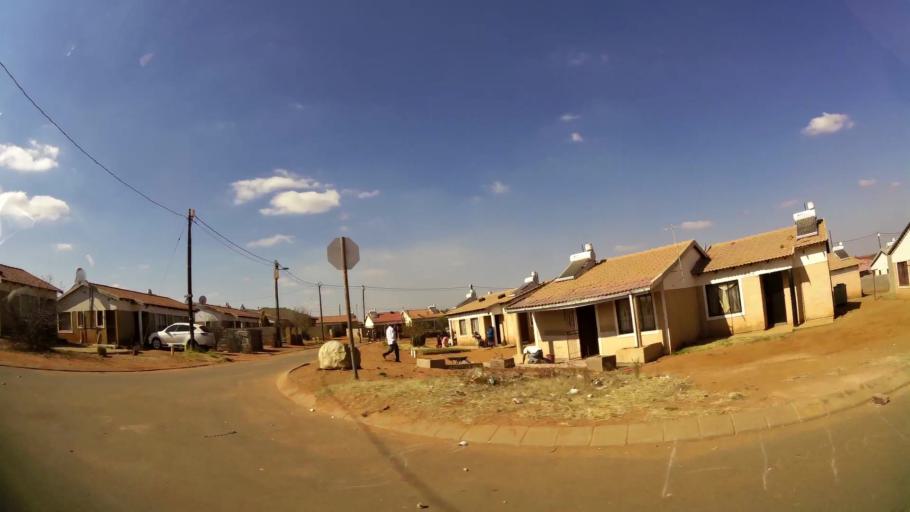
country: ZA
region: Gauteng
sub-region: West Rand District Municipality
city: Randfontein
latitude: -26.1712
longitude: 27.7765
